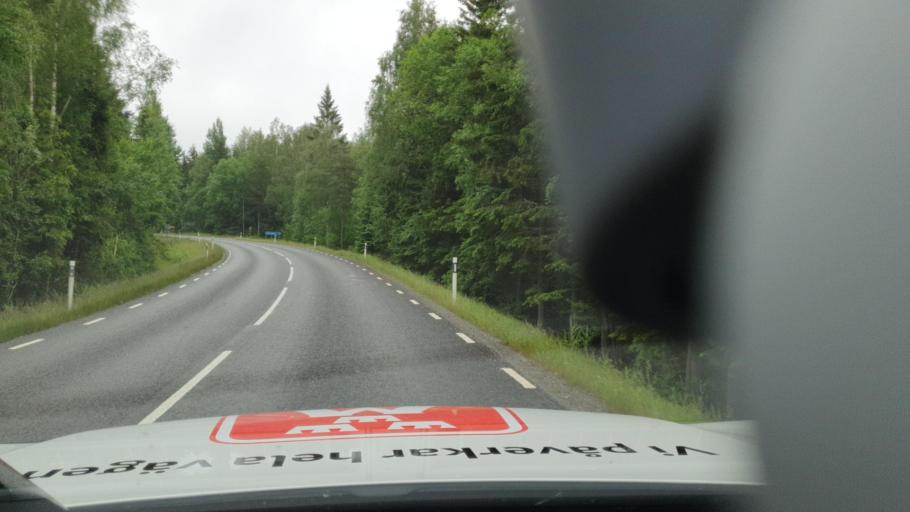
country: SE
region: Vaermland
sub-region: Kristinehamns Kommun
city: Bjorneborg
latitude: 59.2195
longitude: 14.3206
